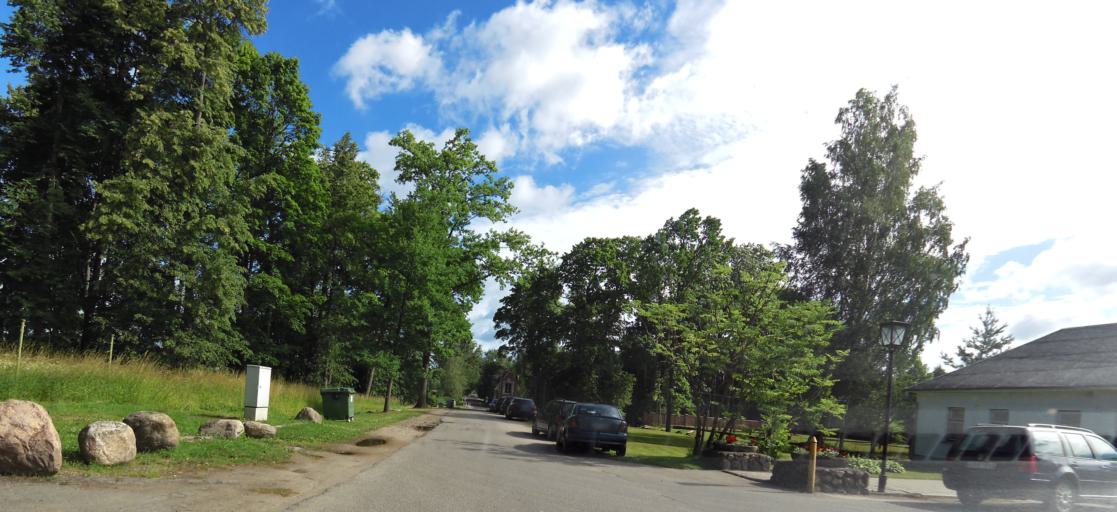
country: LT
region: Panevezys
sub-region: Birzai
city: Birzai
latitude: 56.2212
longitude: 24.7696
